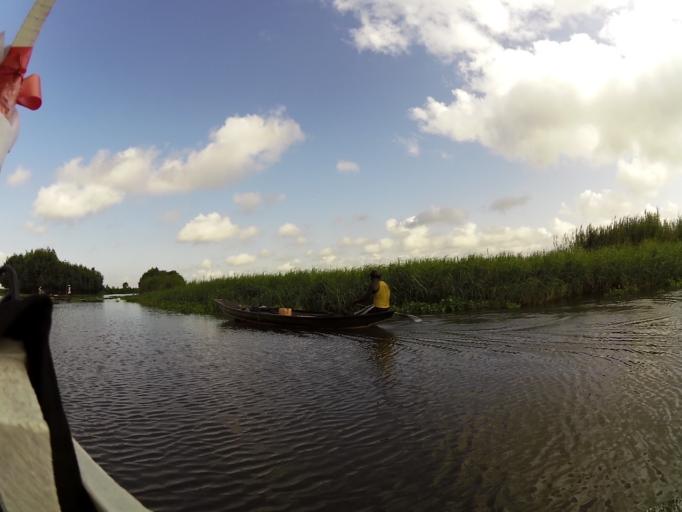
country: BJ
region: Queme
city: Porto-Novo
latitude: 6.4664
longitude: 2.5712
